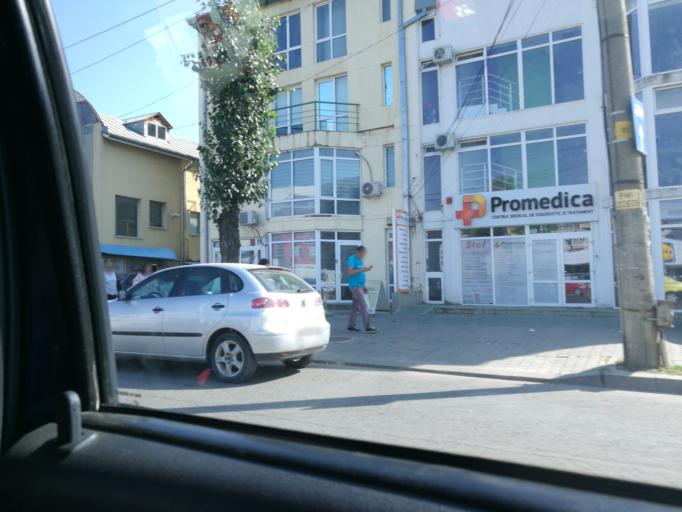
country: RO
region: Iasi
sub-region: Municipiul Iasi
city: Iasi
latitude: 47.1722
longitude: 27.5582
